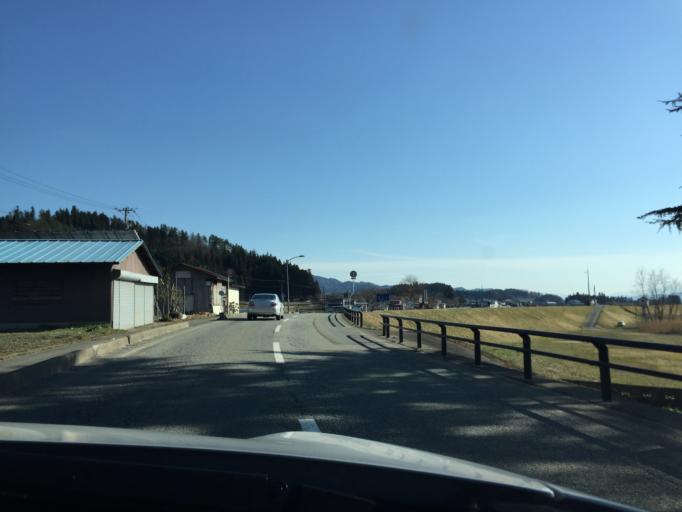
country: JP
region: Yamagata
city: Nagai
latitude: 38.1999
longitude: 140.1039
